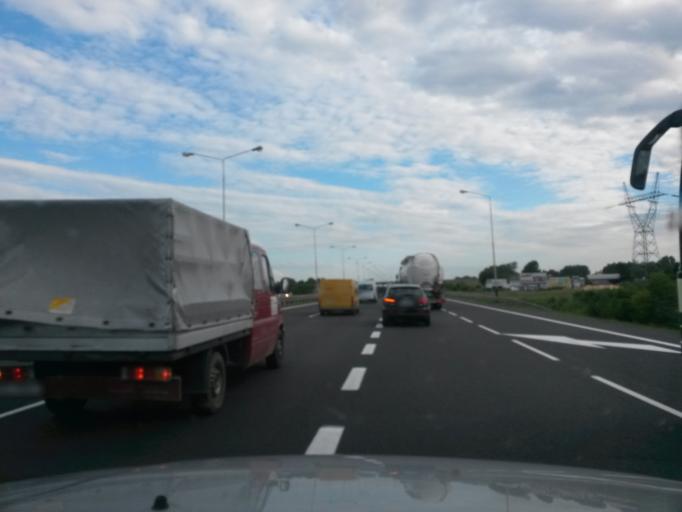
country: PL
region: Lodz Voivodeship
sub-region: Piotrkow Trybunalski
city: Piotrkow Trybunalski
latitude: 51.4305
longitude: 19.6410
